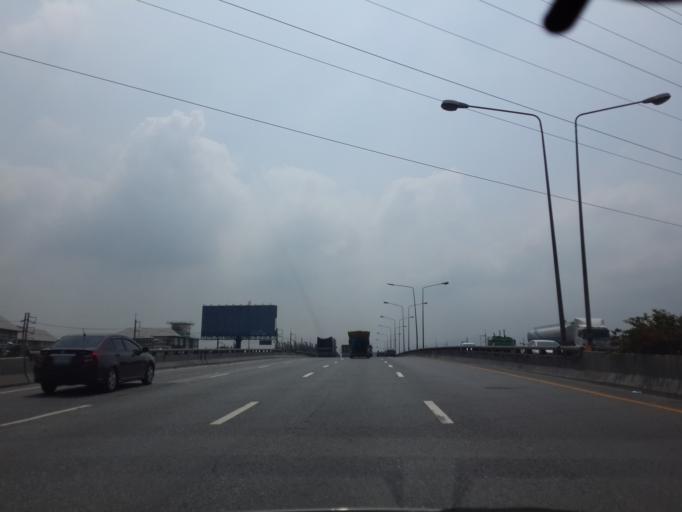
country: TH
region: Chon Buri
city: Chon Buri
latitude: 13.3881
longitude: 101.0146
